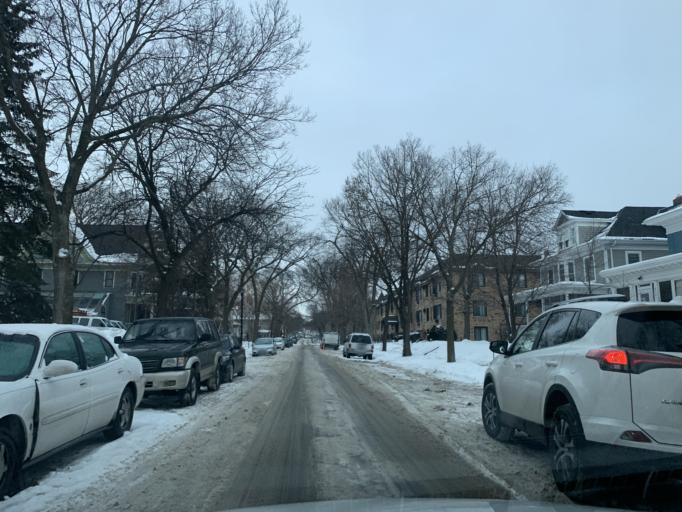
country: US
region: Minnesota
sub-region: Hennepin County
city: Minneapolis
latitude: 44.9597
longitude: -93.2918
